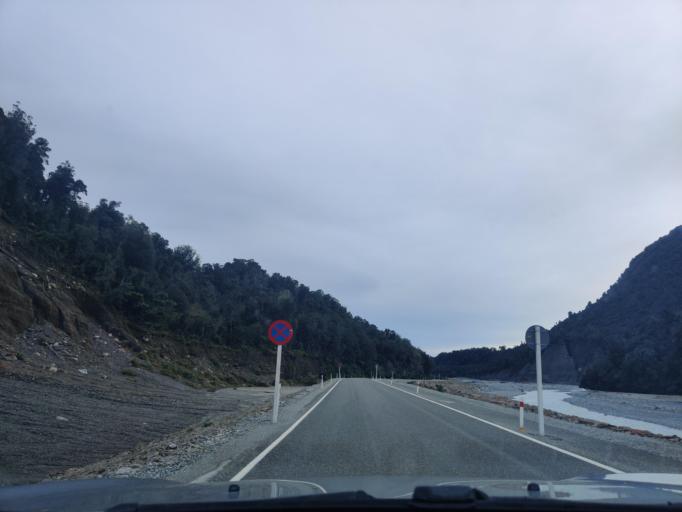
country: NZ
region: West Coast
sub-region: Westland District
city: Hokitika
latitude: -43.4050
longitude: 170.1780
